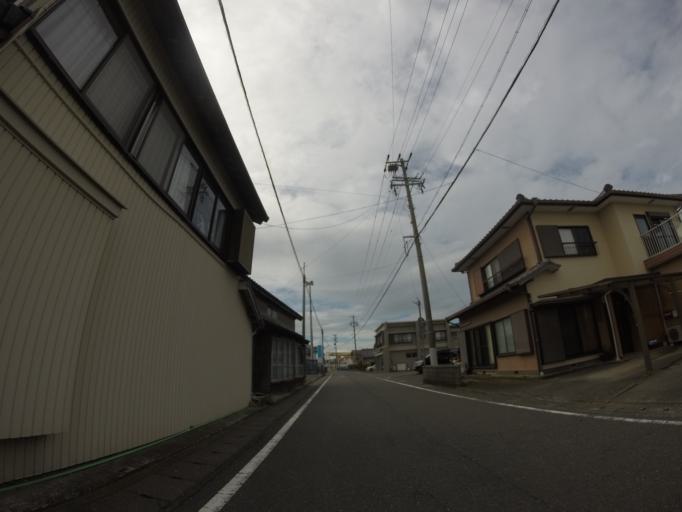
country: JP
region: Shizuoka
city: Oyama
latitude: 34.6069
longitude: 138.2125
